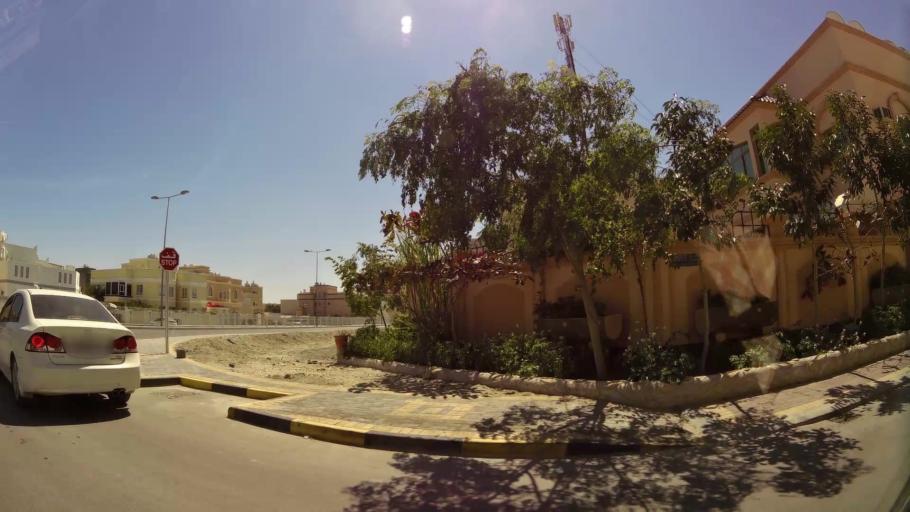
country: BH
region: Muharraq
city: Al Hadd
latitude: 26.2799
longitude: 50.6426
